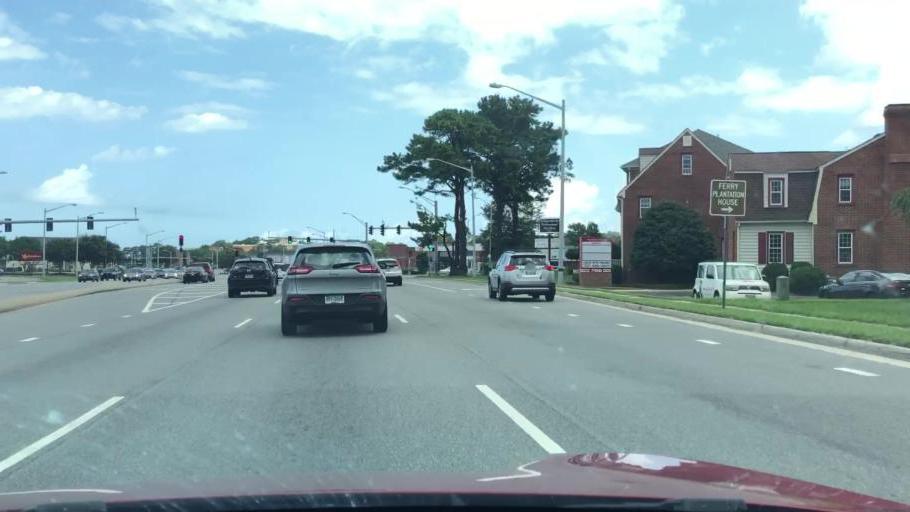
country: US
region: Virginia
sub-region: City of Chesapeake
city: Chesapeake
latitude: 36.8614
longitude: -76.1324
